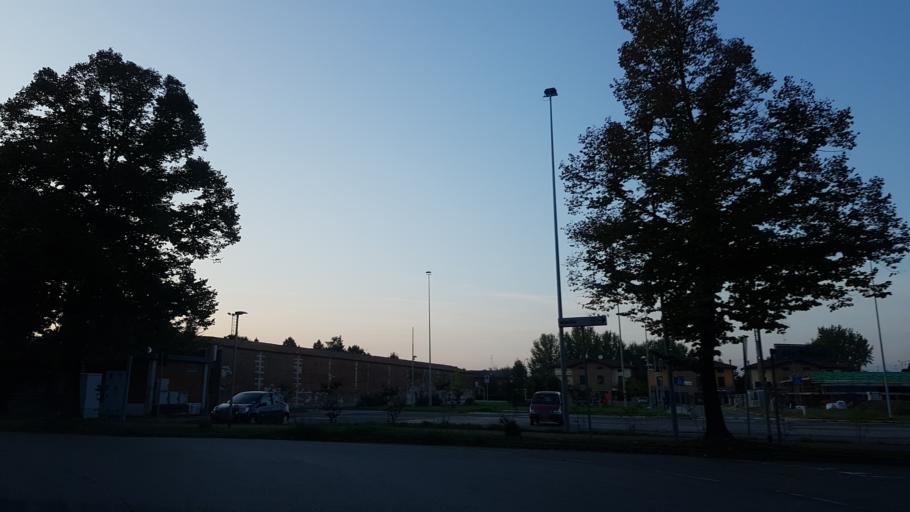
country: IT
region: Emilia-Romagna
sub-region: Provincia di Modena
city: Camposanto
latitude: 44.7895
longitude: 11.1389
